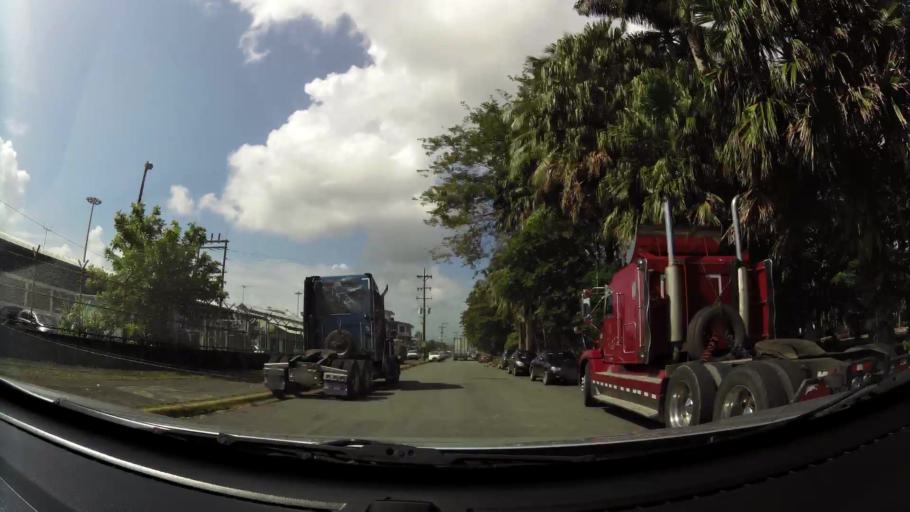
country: CR
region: Limon
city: Limon
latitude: 9.9923
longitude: -83.0247
